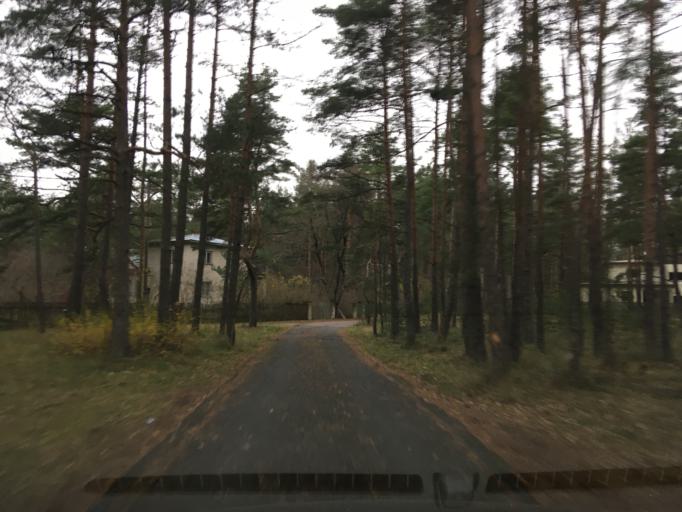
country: EE
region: Harju
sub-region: Tallinna linn
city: Tallinn
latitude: 59.3755
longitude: 24.6997
